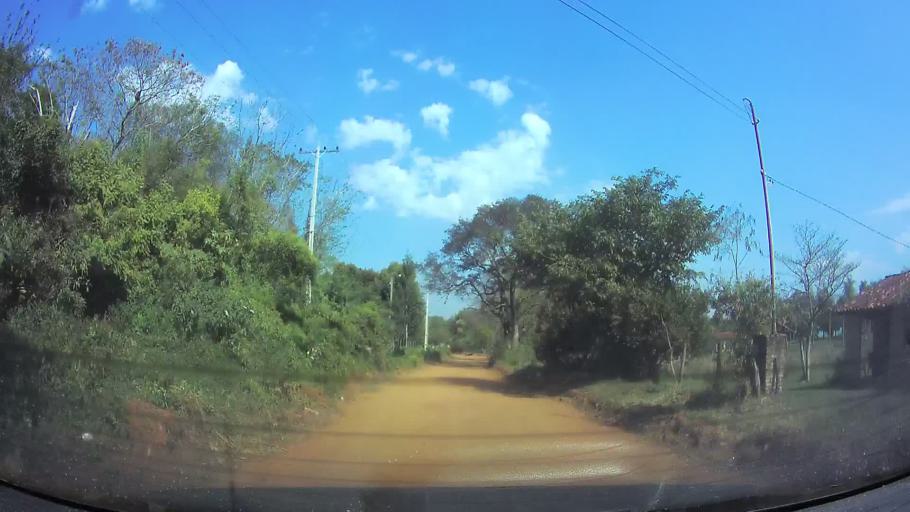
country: PY
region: Central
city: Limpio
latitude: -25.2266
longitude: -57.4400
